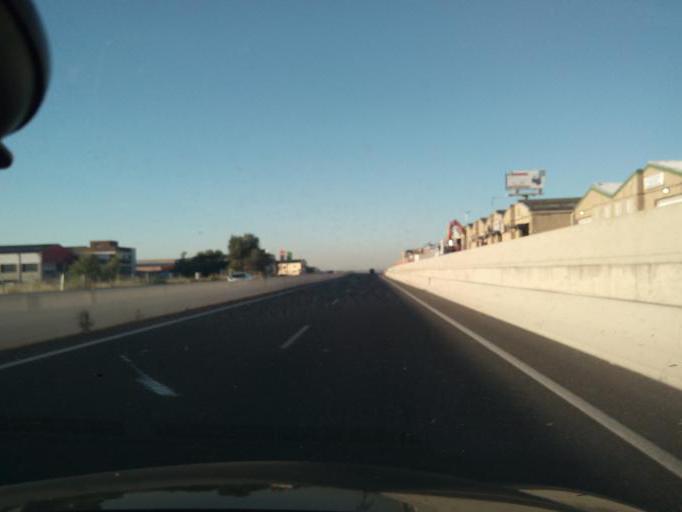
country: ES
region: Madrid
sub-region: Provincia de Madrid
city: Ajalvir
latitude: 40.5138
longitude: -3.4807
